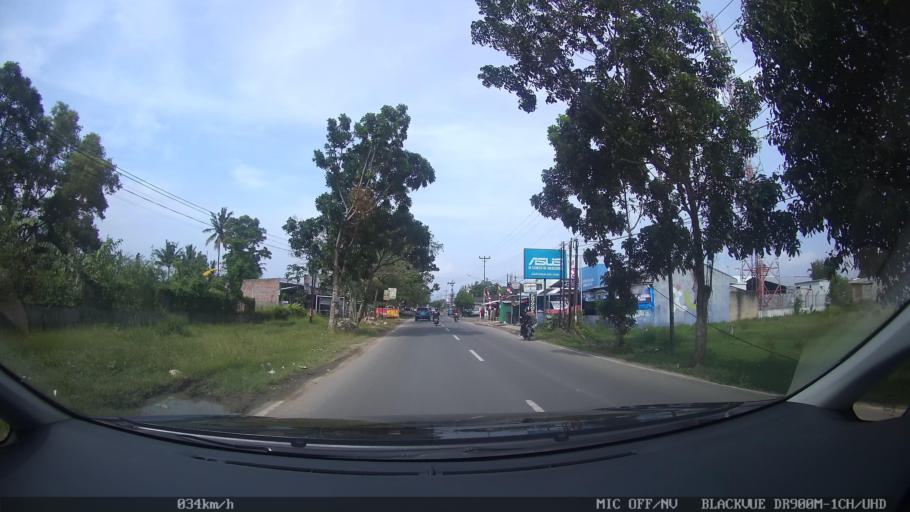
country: ID
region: Lampung
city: Kedaton
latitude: -5.3806
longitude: 105.3008
